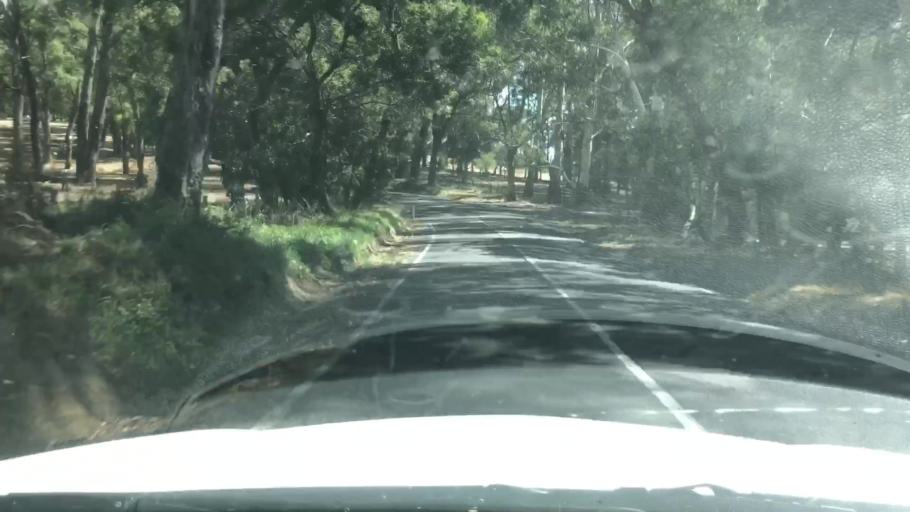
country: AU
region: Victoria
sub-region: Yarra Ranges
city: Macclesfield
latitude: -37.8266
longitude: 145.4911
